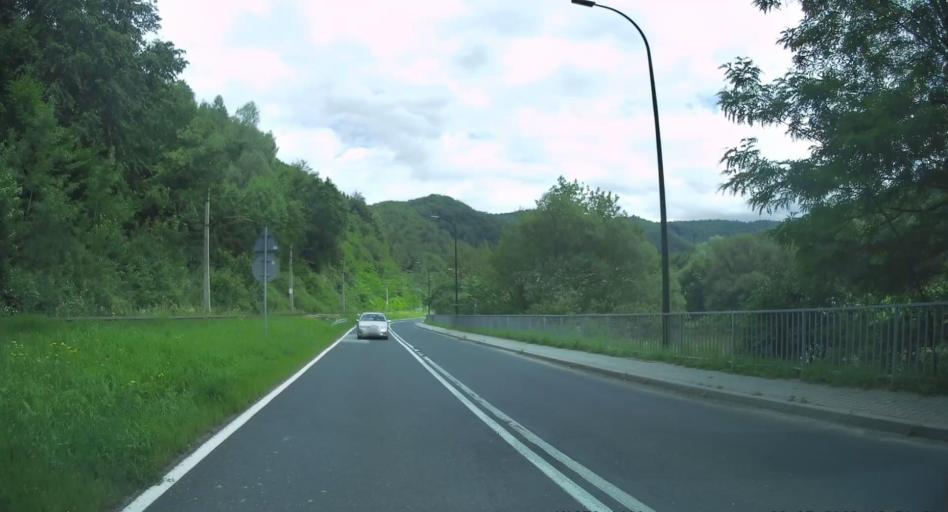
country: PL
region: Lesser Poland Voivodeship
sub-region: Powiat nowosadecki
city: Muszyna
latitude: 49.3636
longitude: 20.7958
